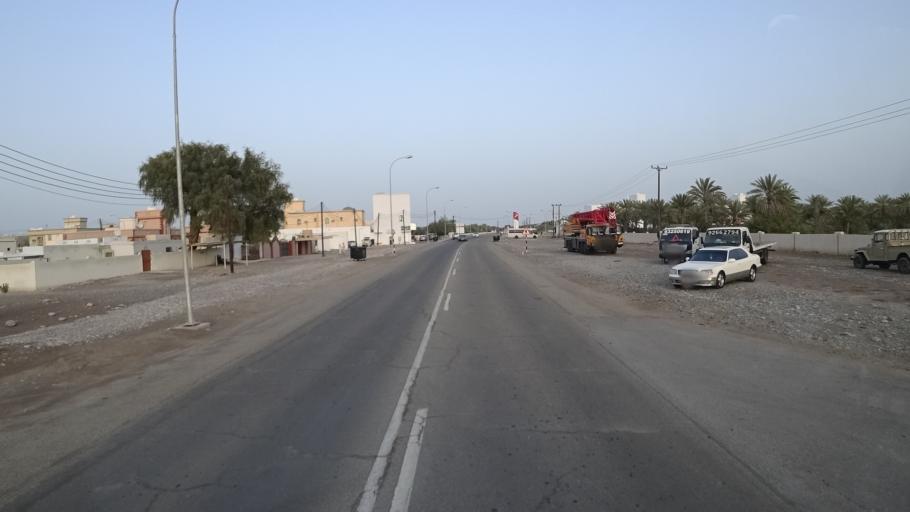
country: OM
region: Muhafazat Masqat
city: Muscat
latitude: 23.2063
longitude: 58.9650
